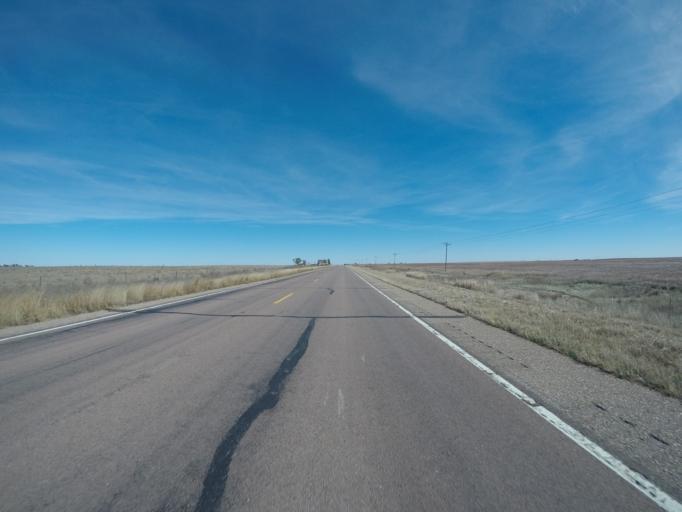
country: US
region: Colorado
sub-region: Yuma County
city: Yuma
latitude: 39.6559
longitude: -102.6568
